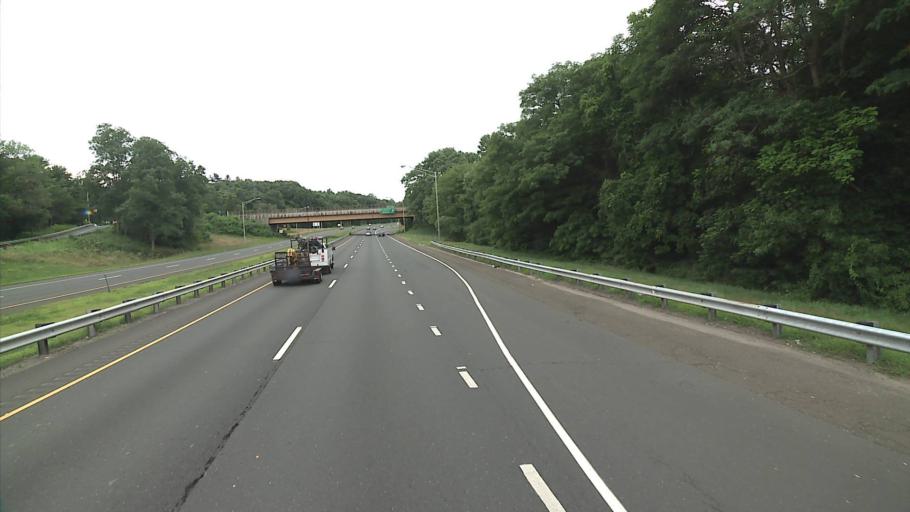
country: US
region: Connecticut
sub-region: Fairfield County
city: Shelton
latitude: 41.3060
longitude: -73.0990
